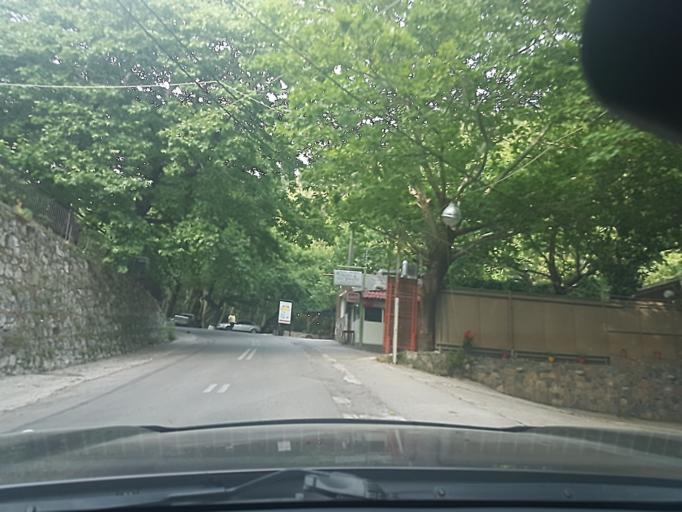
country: GR
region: Central Greece
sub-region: Nomos Evvoias
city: Yimnon
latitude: 38.5863
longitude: 23.8449
